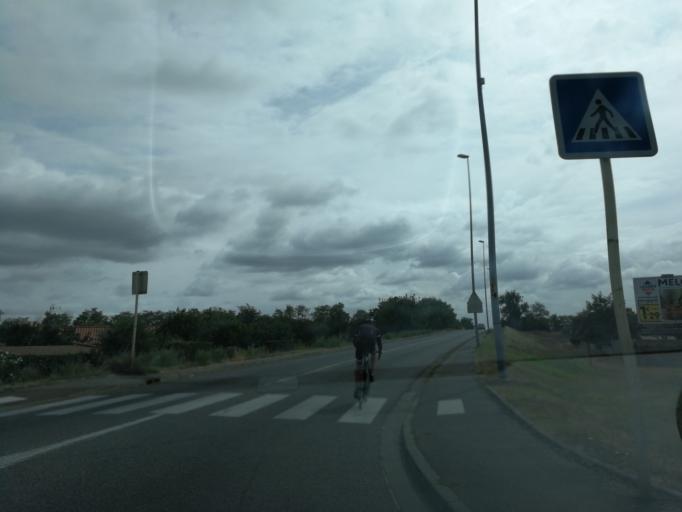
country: FR
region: Midi-Pyrenees
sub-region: Departement de la Haute-Garonne
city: Saint-Alban
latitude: 43.6884
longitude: 1.4094
